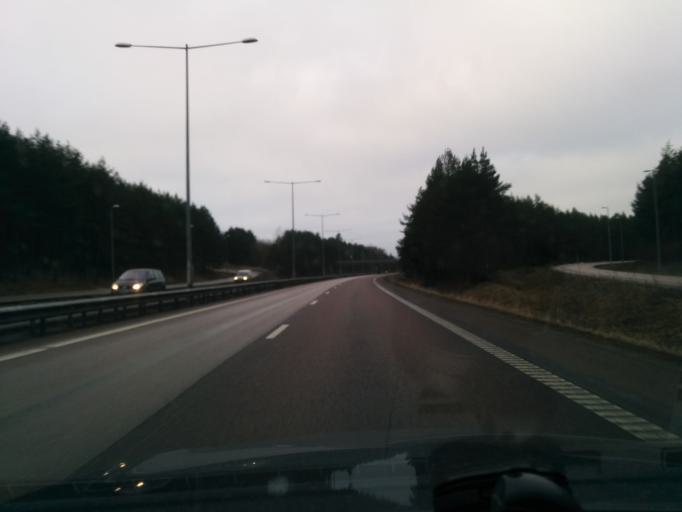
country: SE
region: Vaestmanland
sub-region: Vasteras
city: Tillberga
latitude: 59.6105
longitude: 16.6338
